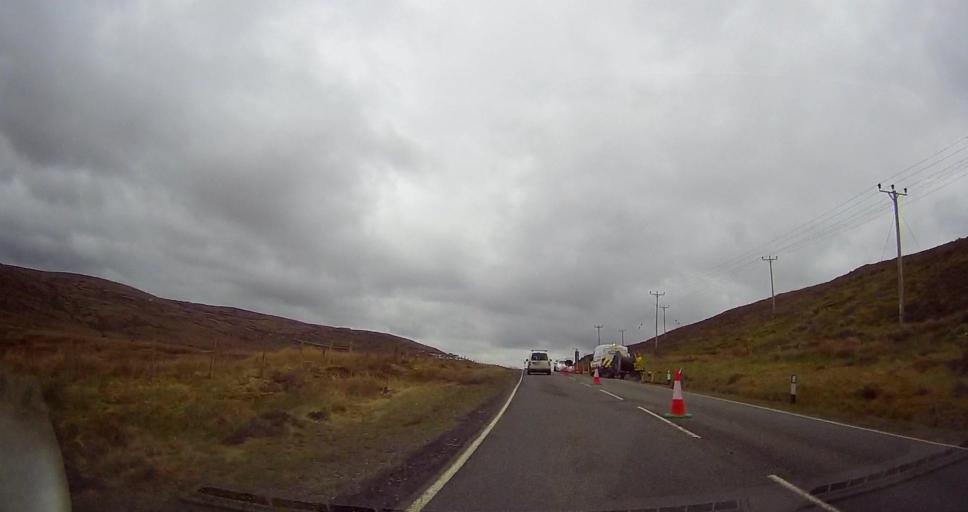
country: GB
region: Scotland
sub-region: Shetland Islands
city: Lerwick
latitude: 60.3342
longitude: -1.2539
